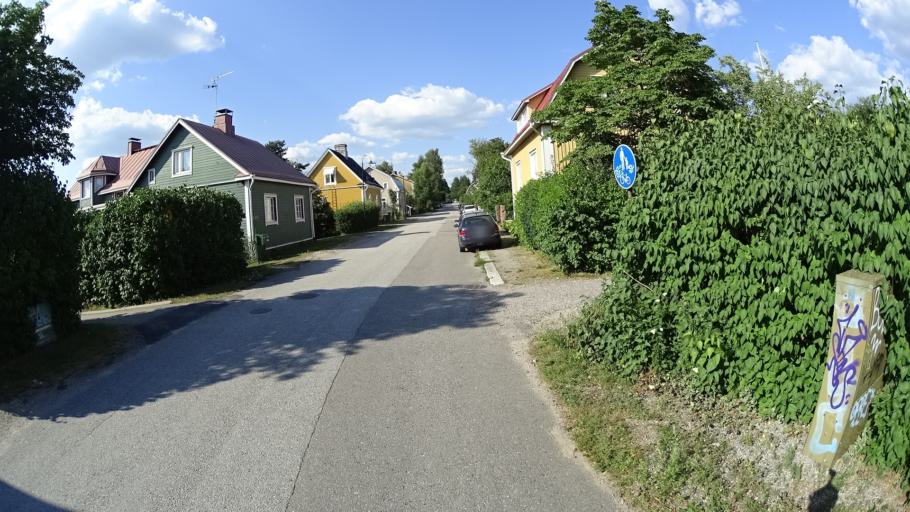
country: FI
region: Uusimaa
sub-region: Porvoo
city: Porvoo
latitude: 60.3984
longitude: 25.6730
